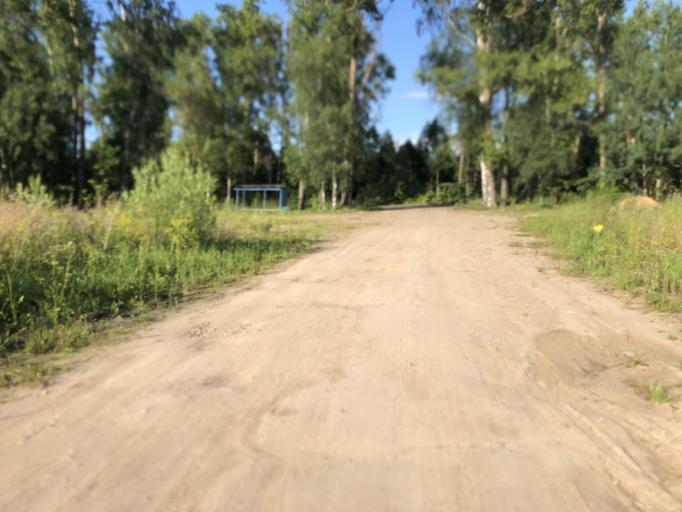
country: RU
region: Tverskaya
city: Rzhev
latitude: 56.2688
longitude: 34.2478
